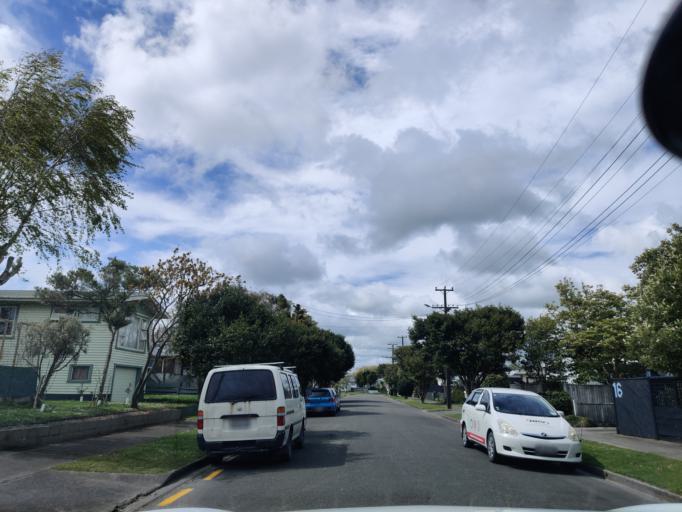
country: NZ
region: Manawatu-Wanganui
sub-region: Palmerston North City
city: Palmerston North
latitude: -40.3812
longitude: 175.5889
